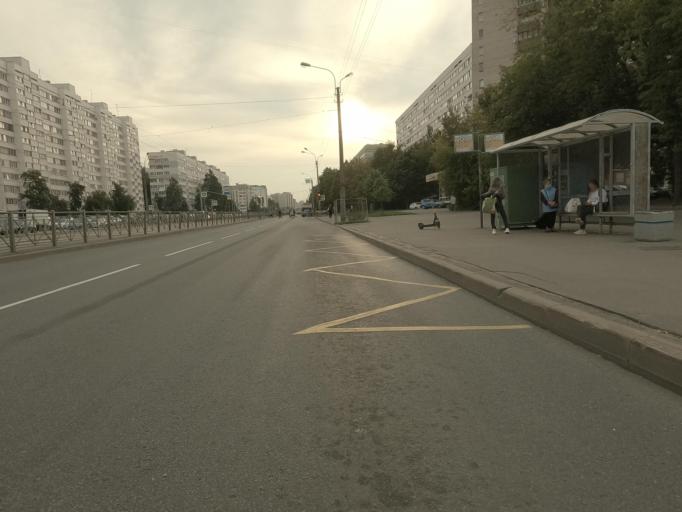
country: RU
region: St.-Petersburg
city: Dachnoye
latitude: 59.8597
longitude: 30.2477
